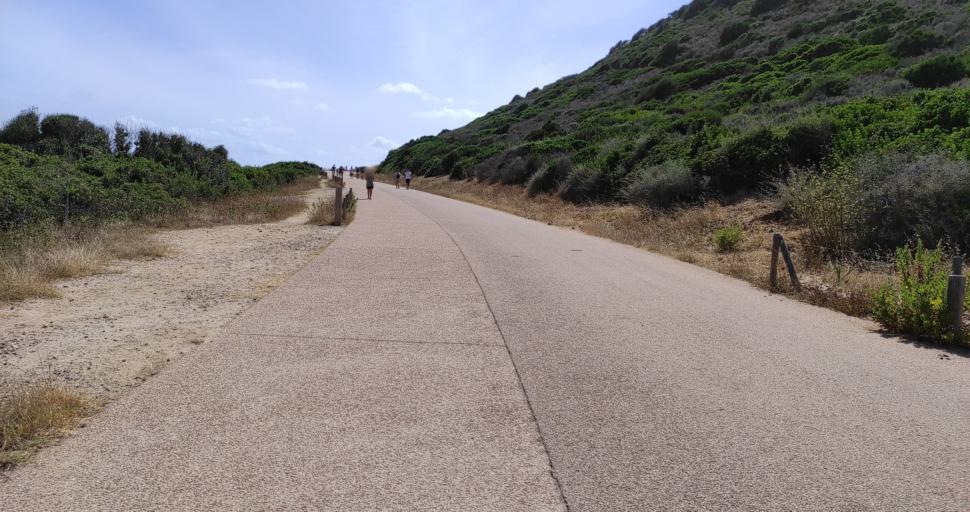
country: FR
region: Corsica
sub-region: Departement de la Corse-du-Sud
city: Ajaccio
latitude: 41.9004
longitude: 8.6159
